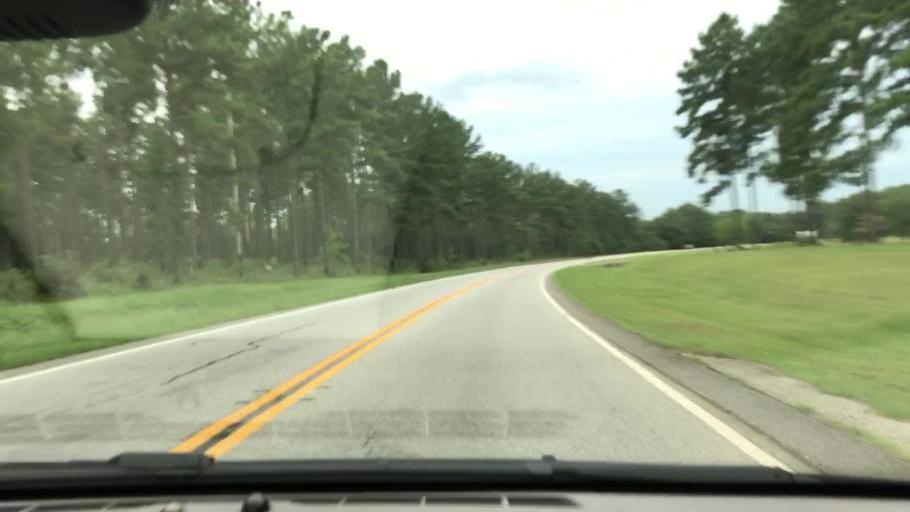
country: US
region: Georgia
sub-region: Early County
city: Blakely
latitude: 31.2813
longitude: -85.0723
